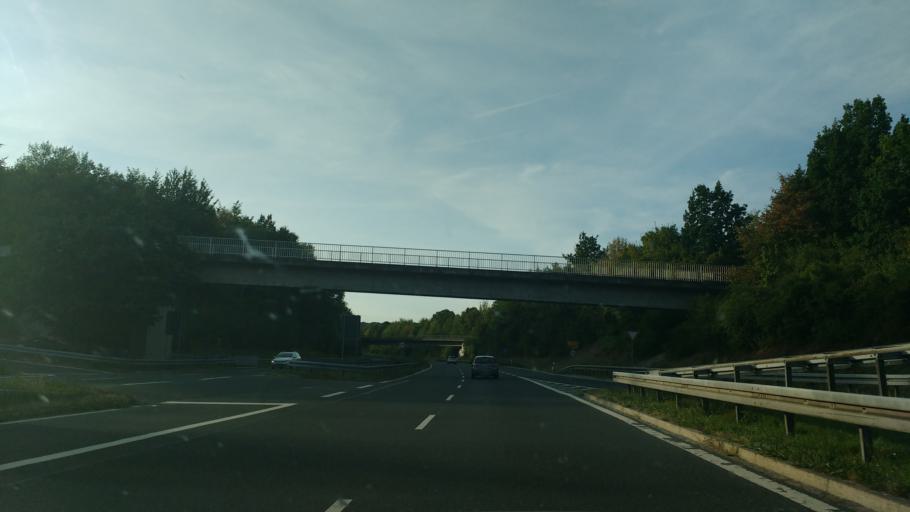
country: DE
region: Bavaria
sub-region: Regierungsbezirk Mittelfranken
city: Zirndorf
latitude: 49.4377
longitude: 10.9821
